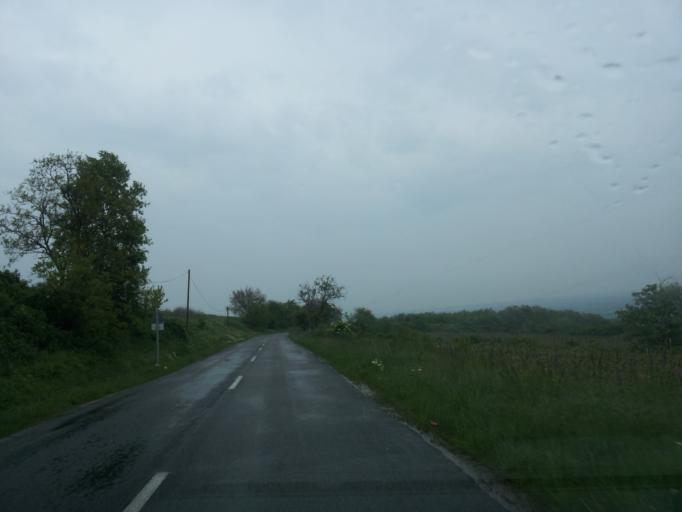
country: HU
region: Tolna
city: Szekszard
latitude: 46.2908
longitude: 18.6753
